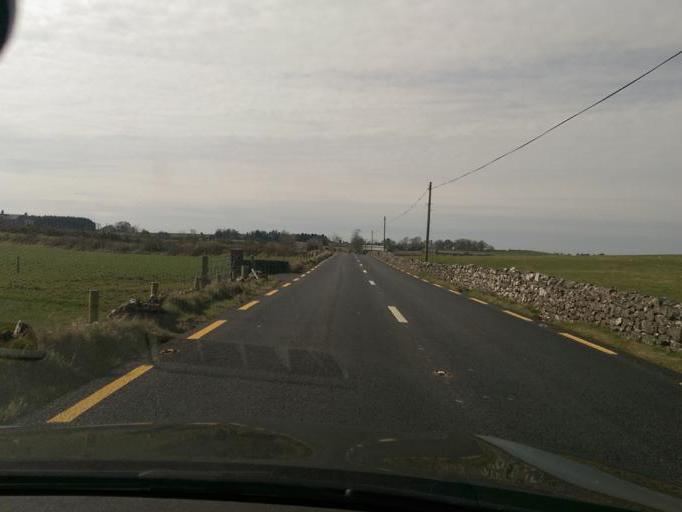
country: IE
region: Connaught
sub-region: County Galway
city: Athenry
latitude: 53.4816
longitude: -8.5981
